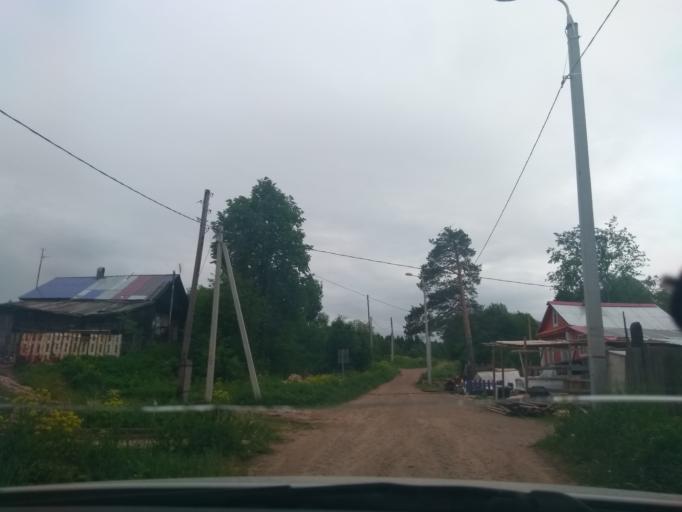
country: RU
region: Perm
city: Perm
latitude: 57.9900
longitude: 56.3377
